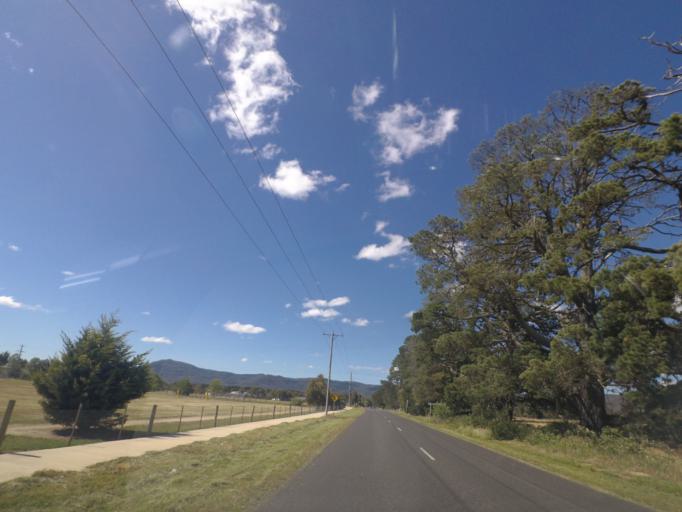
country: AU
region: Victoria
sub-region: Hume
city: Sunbury
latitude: -37.4567
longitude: 144.5992
